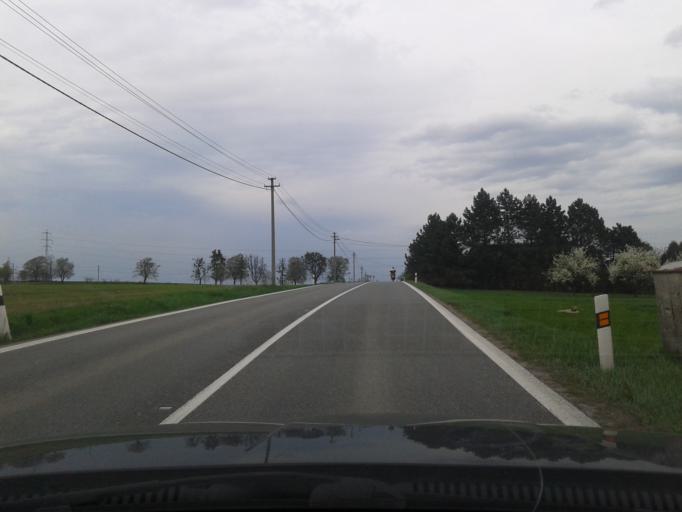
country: CZ
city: Sedliste
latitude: 49.7101
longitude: 18.3679
